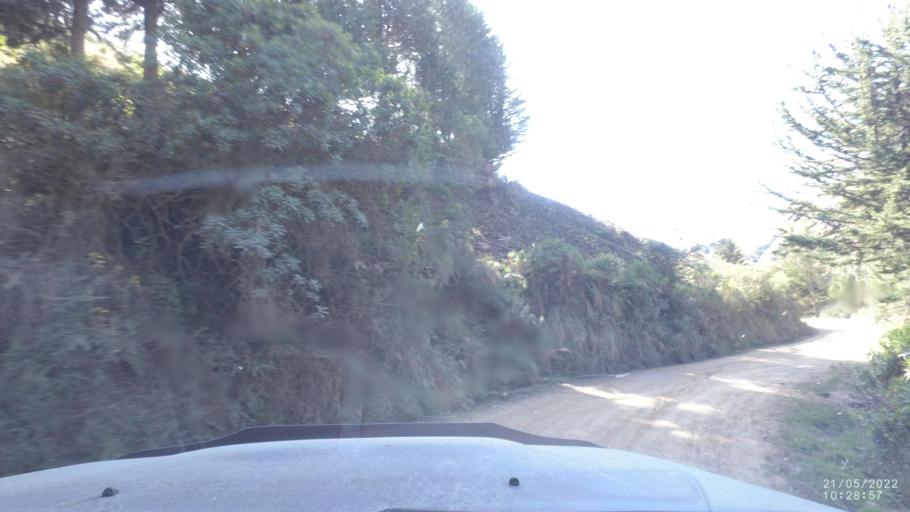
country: BO
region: Cochabamba
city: Colomi
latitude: -17.3208
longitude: -65.9402
